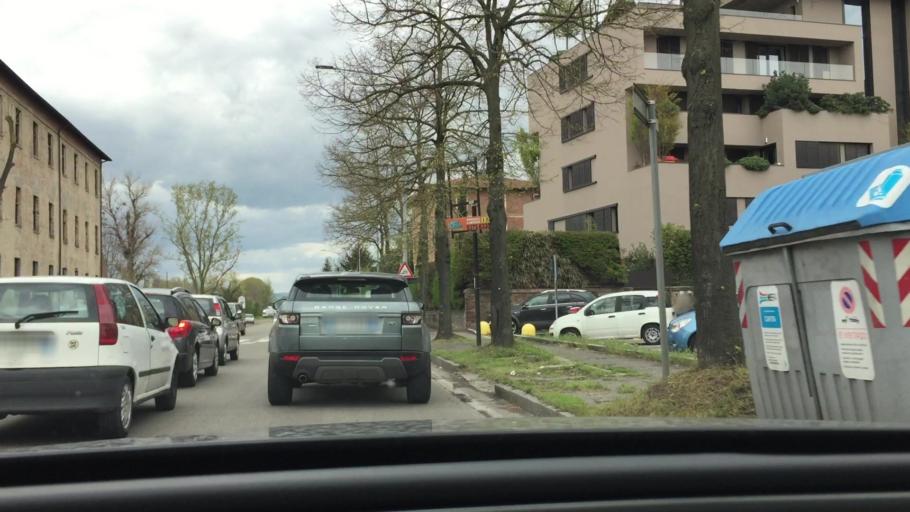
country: IT
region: Emilia-Romagna
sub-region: Provincia di Modena
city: Modena
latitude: 44.6293
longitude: 10.8981
